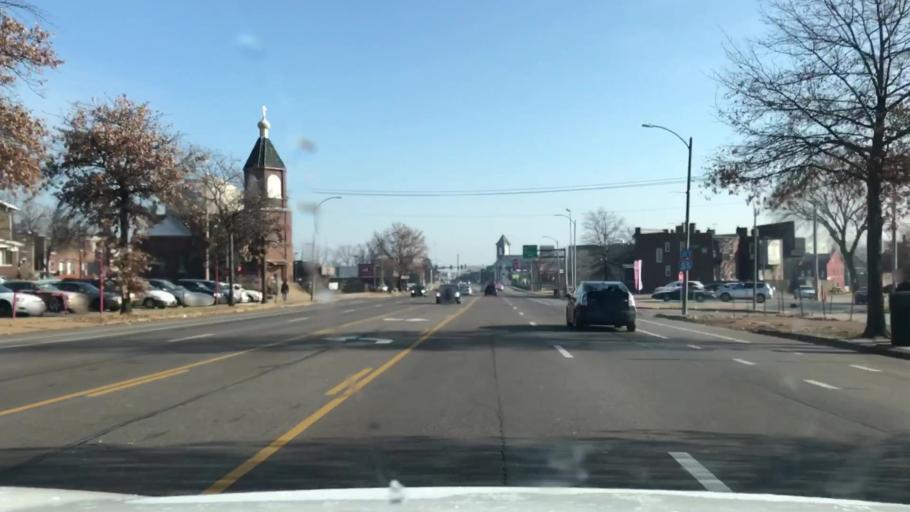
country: US
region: Missouri
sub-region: City of Saint Louis
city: St. Louis
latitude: 38.6076
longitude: -90.2153
